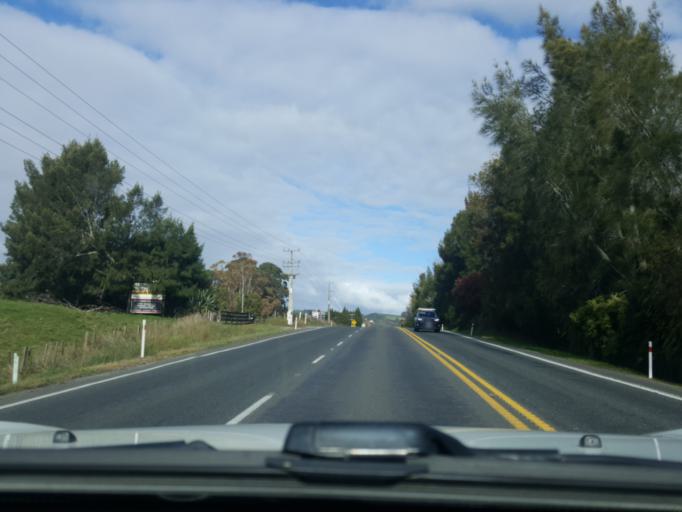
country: NZ
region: Bay of Plenty
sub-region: Tauranga City
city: Tauranga
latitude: -37.6737
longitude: 176.0228
